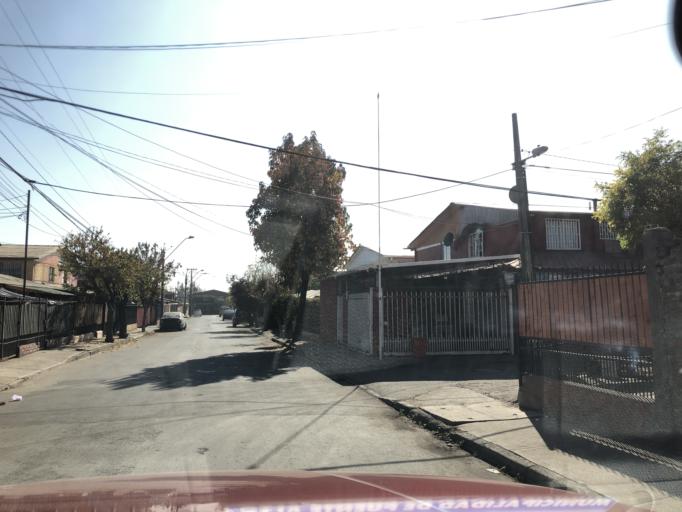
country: CL
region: Santiago Metropolitan
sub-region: Provincia de Cordillera
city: Puente Alto
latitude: -33.5639
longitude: -70.5665
